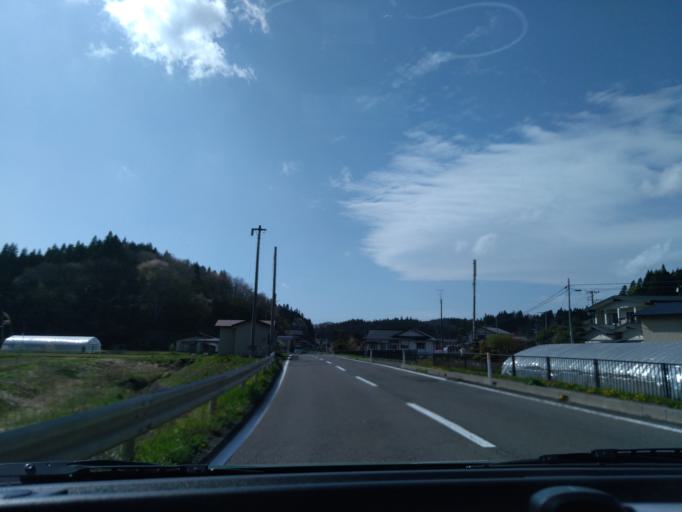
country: JP
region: Akita
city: Akita
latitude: 39.7116
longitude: 140.2031
